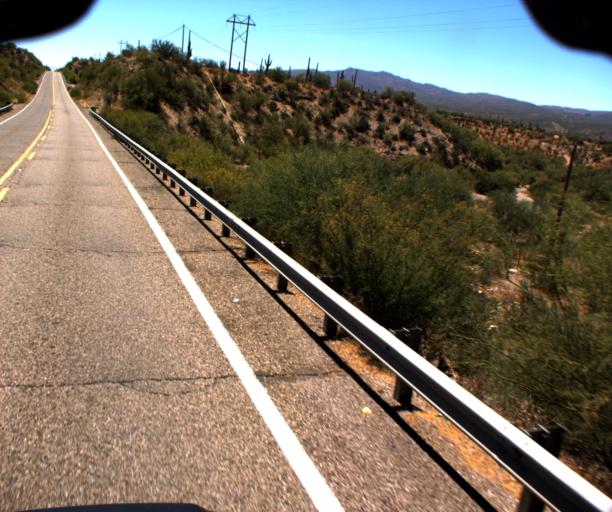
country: US
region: Arizona
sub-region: Pinal County
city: Kearny
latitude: 33.0748
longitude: -110.9213
